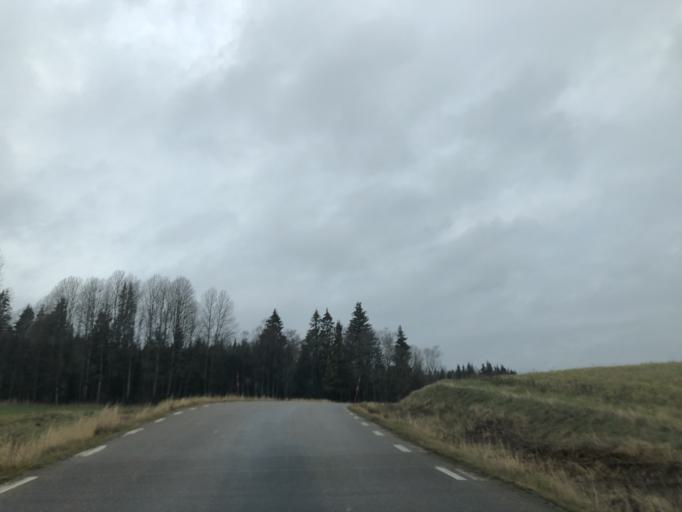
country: SE
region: Vaestra Goetaland
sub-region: Ulricehamns Kommun
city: Ulricehamn
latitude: 57.8896
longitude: 13.5111
